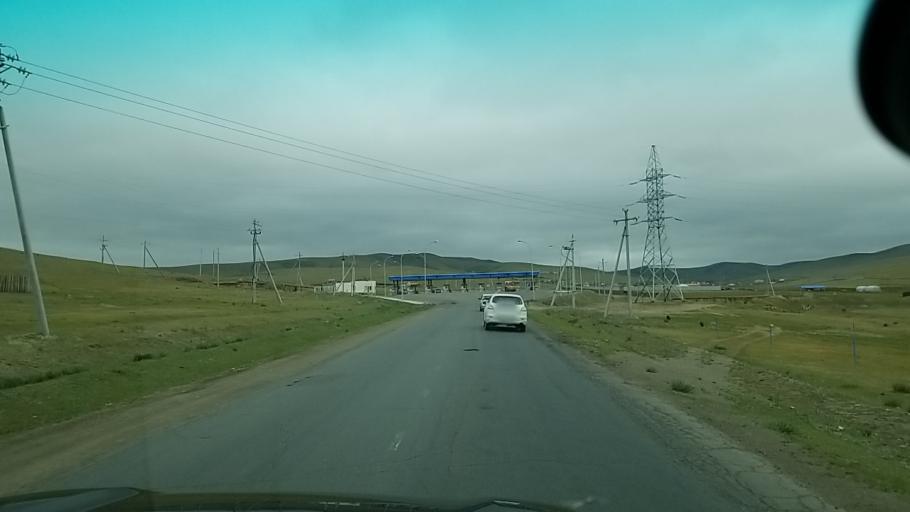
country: MN
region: Ulaanbaatar
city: Ulaanbaatar
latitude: 47.9241
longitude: 106.6230
